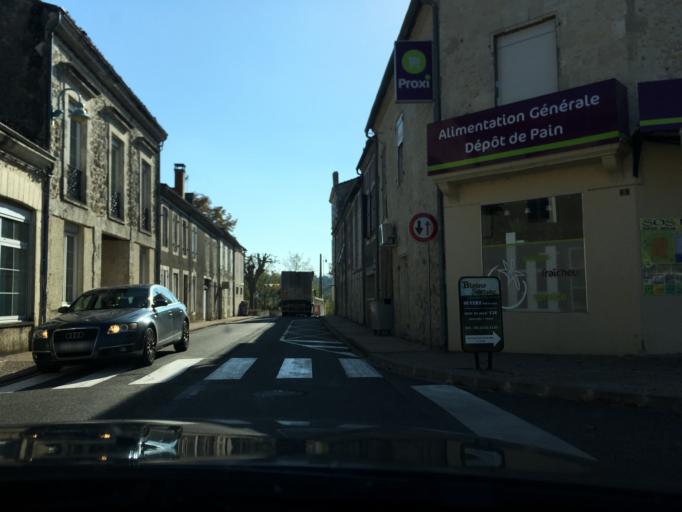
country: FR
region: Midi-Pyrenees
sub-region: Departement du Gers
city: Montreal
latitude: 44.0425
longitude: 0.1424
